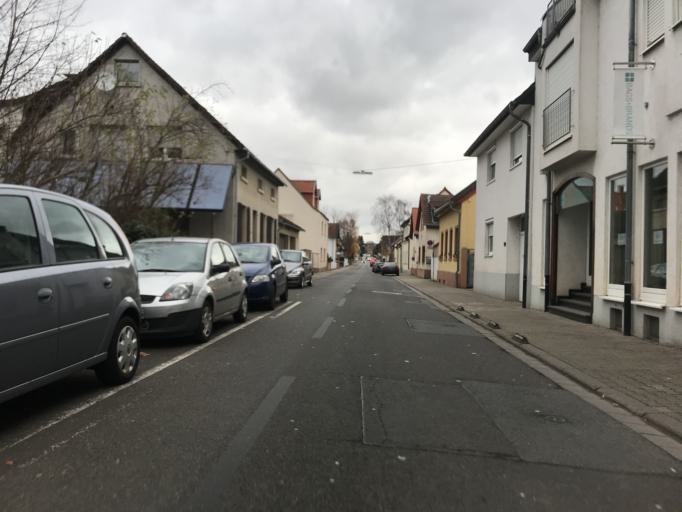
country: DE
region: Rheinland-Pfalz
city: Nieder-Olm
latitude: 49.9122
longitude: 8.2029
